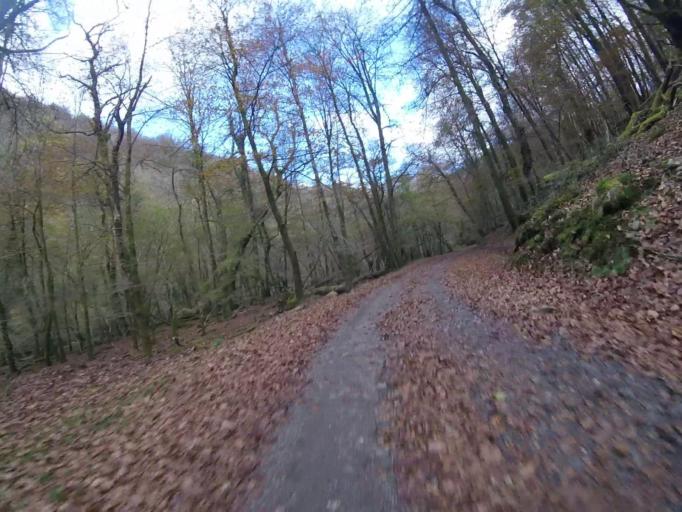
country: ES
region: Navarre
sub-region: Provincia de Navarra
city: Goizueta
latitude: 43.1982
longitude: -1.8054
